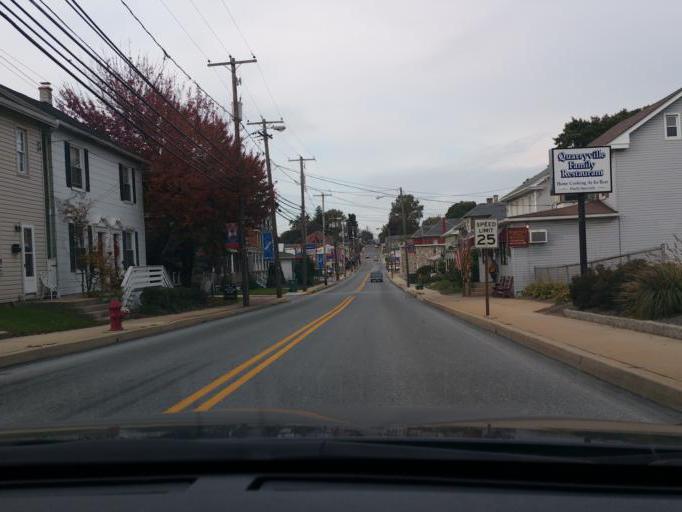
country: US
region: Pennsylvania
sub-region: Lancaster County
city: Quarryville
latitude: 39.8985
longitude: -76.1597
